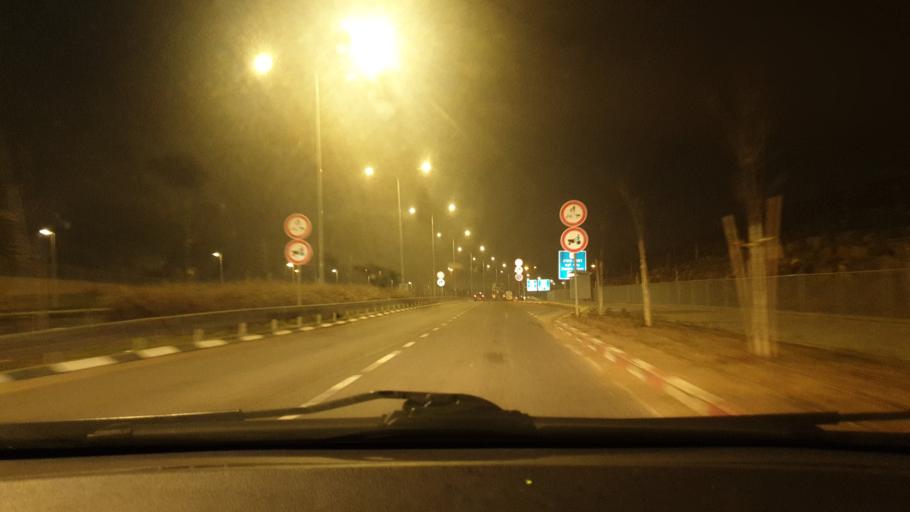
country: IL
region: Central District
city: Ramla
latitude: 31.9297
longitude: 34.8451
